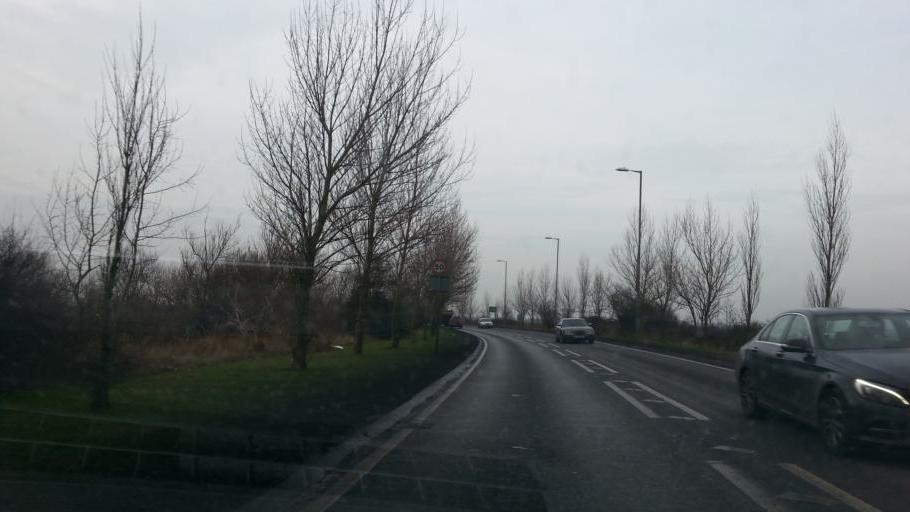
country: GB
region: England
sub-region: Essex
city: South Benfleet
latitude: 51.5380
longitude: 0.5615
